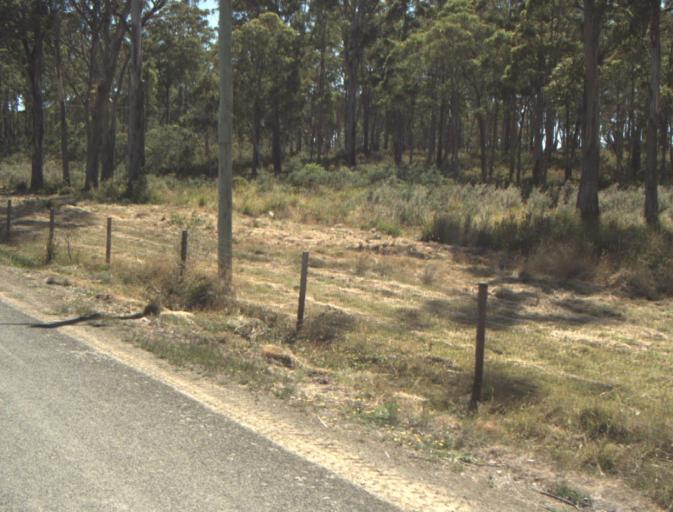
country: AU
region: Tasmania
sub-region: Launceston
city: Newstead
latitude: -41.3834
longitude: 147.2974
